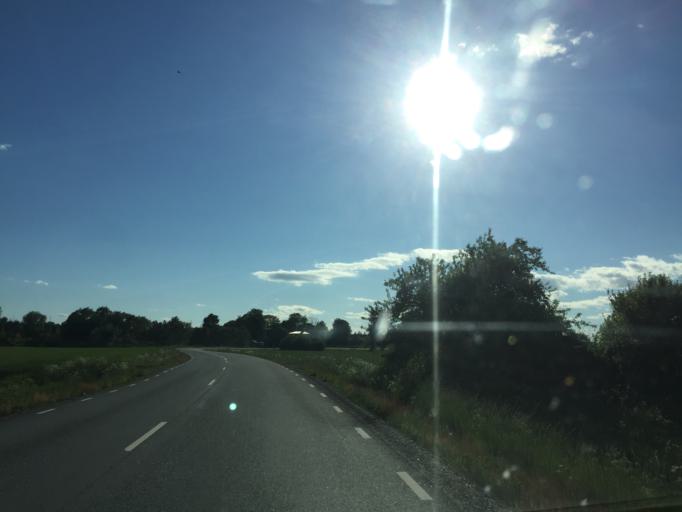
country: SE
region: OErebro
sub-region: Orebro Kommun
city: Orebro
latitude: 59.1968
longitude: 15.2530
